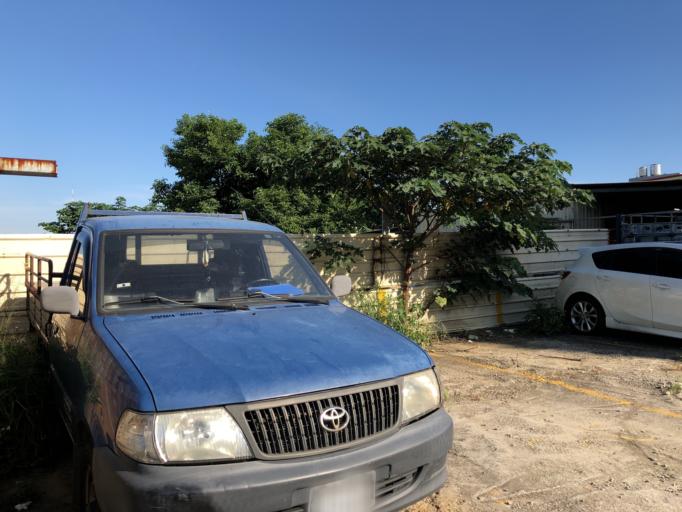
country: TW
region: Taiwan
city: Daxi
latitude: 24.9326
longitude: 121.2267
